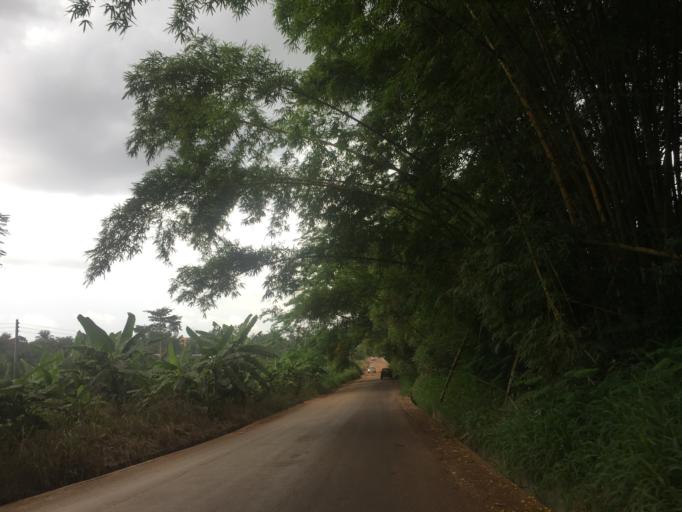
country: GH
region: Ashanti
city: Mamponteng
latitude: 6.6856
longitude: -1.5623
